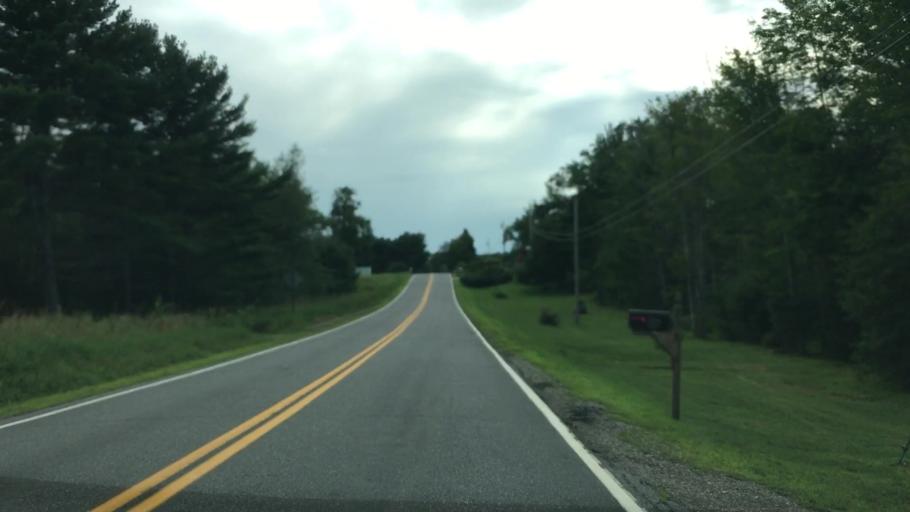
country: US
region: Maine
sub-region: Waldo County
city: Lincolnville
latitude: 44.3210
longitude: -69.0753
